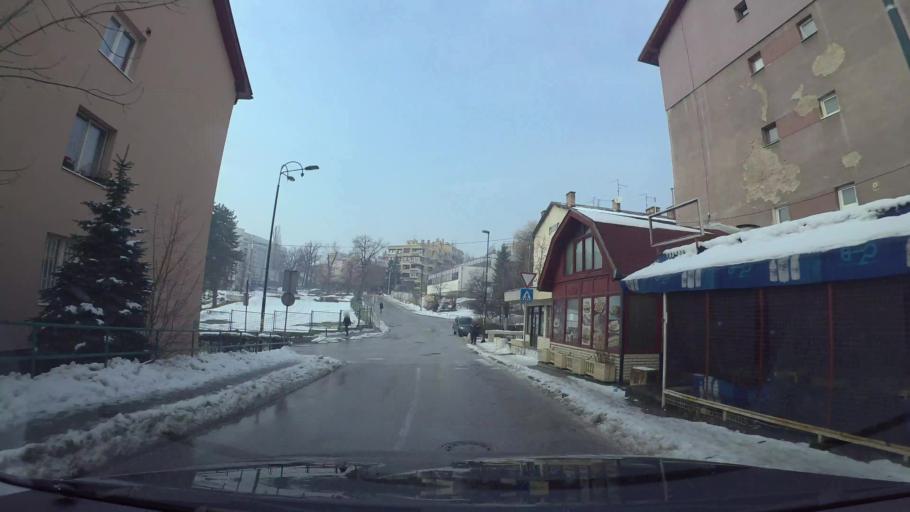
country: BA
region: Federation of Bosnia and Herzegovina
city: Kobilja Glava
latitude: 43.8688
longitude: 18.4192
